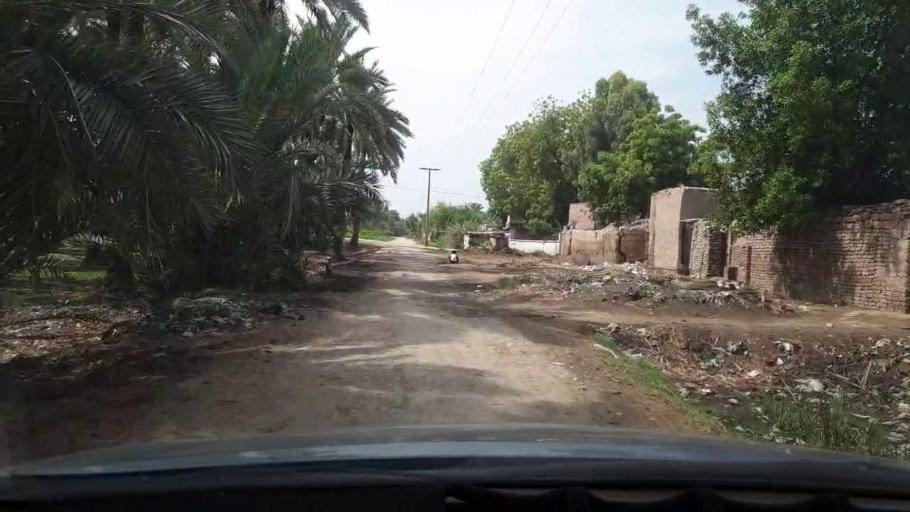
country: PK
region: Sindh
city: Khairpur
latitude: 27.4927
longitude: 68.7546
